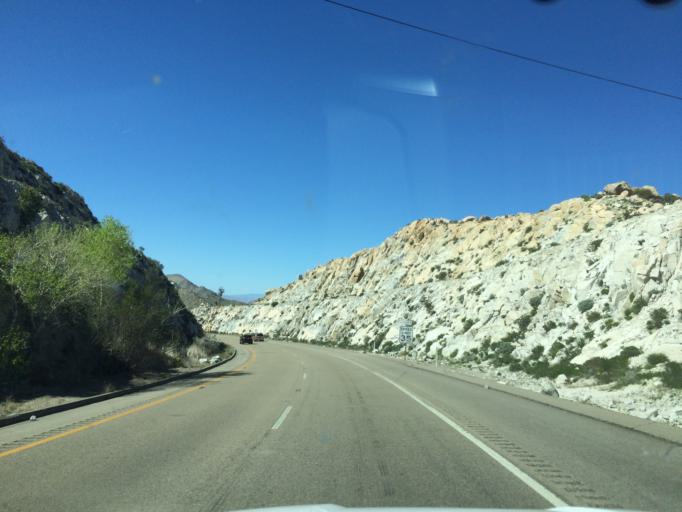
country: MX
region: Baja California
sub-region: Tecate
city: Cereso del Hongo
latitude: 32.6582
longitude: -116.0972
